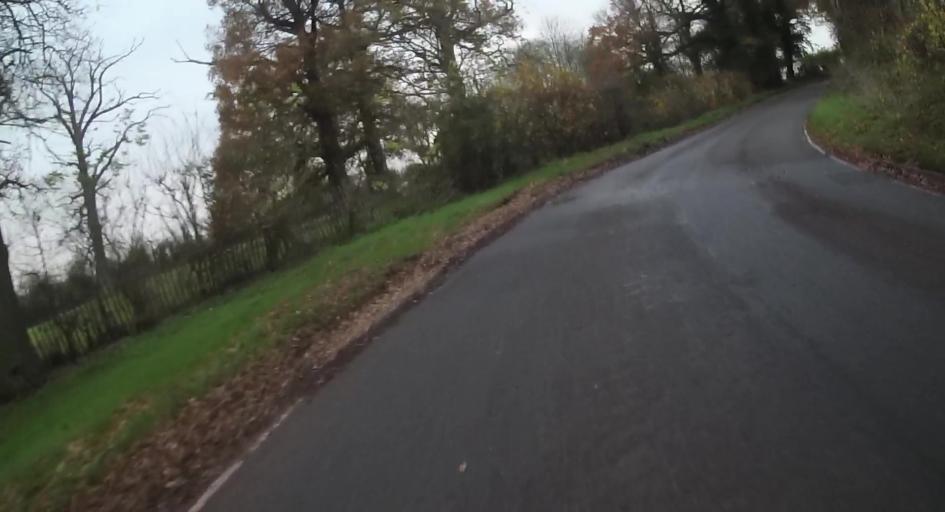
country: GB
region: England
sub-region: Wokingham
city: Swallowfield
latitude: 51.3837
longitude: -0.9368
